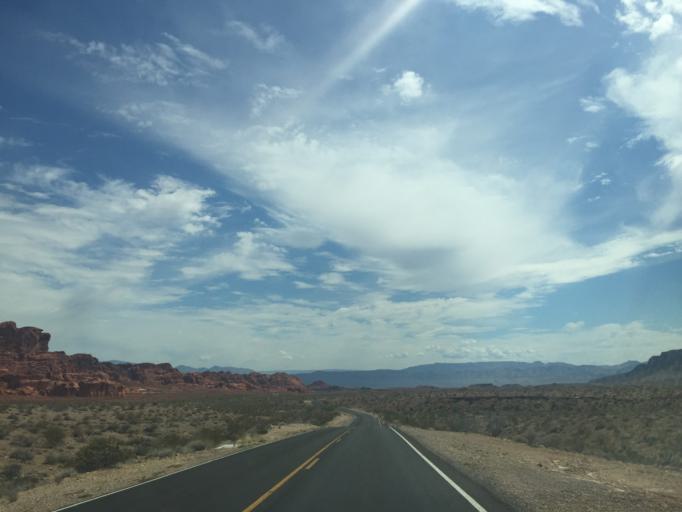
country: US
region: Nevada
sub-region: Clark County
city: Moapa Valley
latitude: 36.4252
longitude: -114.5334
